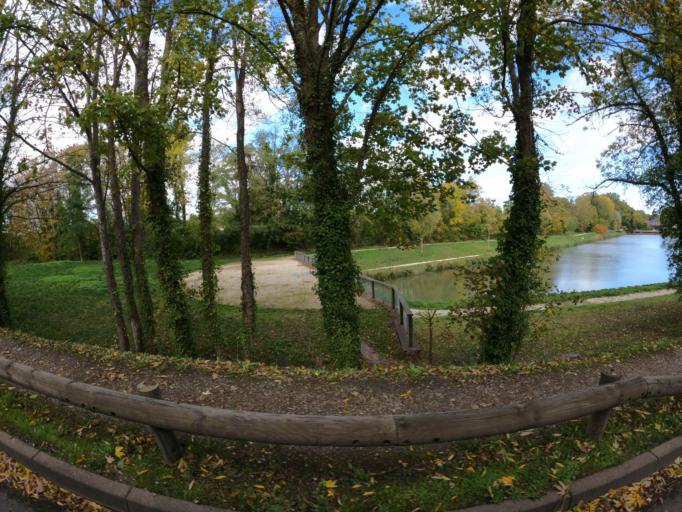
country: FR
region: Ile-de-France
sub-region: Departement de Seine-et-Marne
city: Coupvray
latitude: 48.8957
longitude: 2.7931
